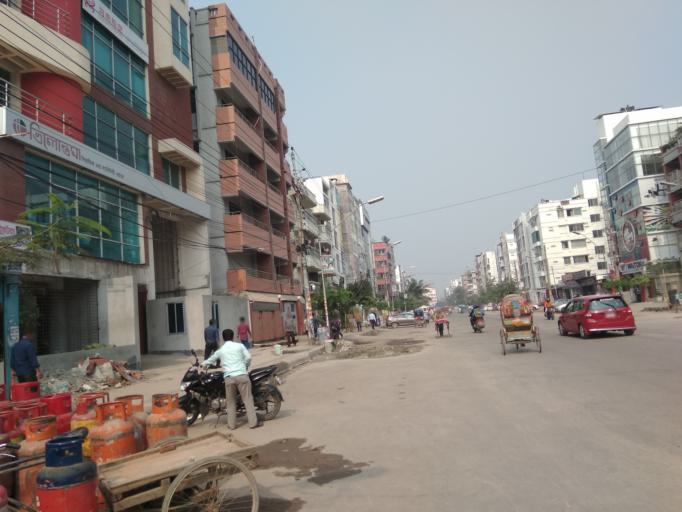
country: BD
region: Dhaka
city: Tungi
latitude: 23.8700
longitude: 90.3839
